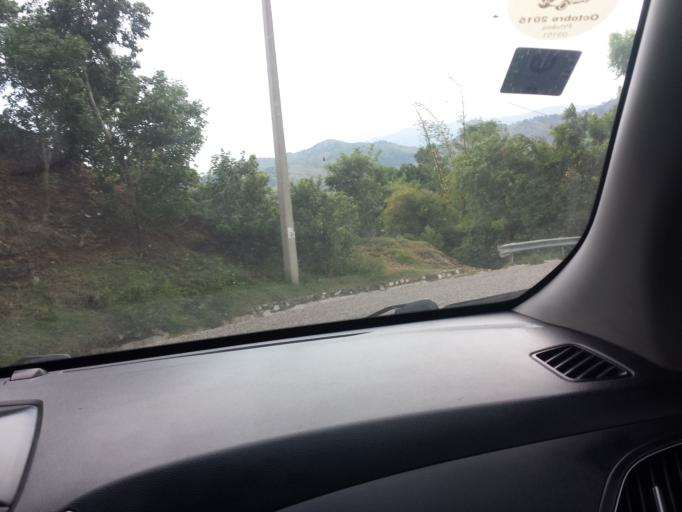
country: HT
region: Ouest
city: Leogane
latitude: 18.3958
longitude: -72.6227
